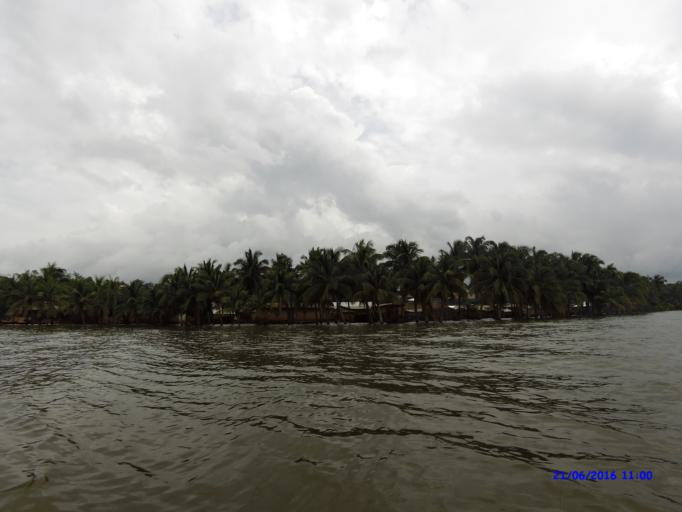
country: BJ
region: Mono
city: Come
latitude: 6.5078
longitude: 1.9657
